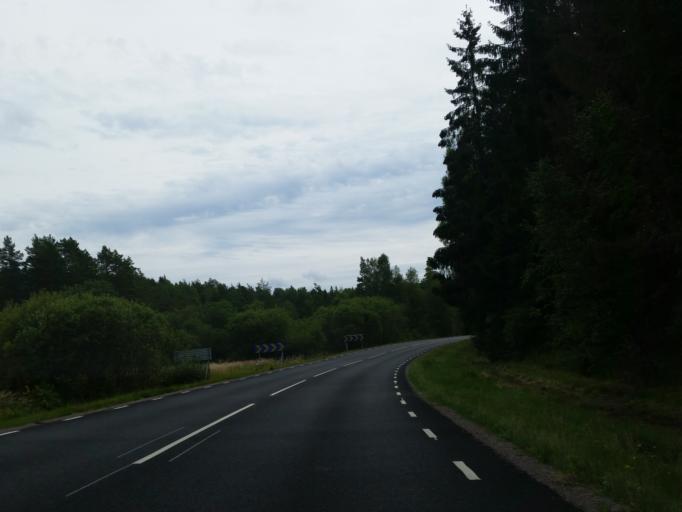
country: SE
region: Soedermanland
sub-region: Strangnas Kommun
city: Mariefred
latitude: 59.2694
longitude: 17.1582
